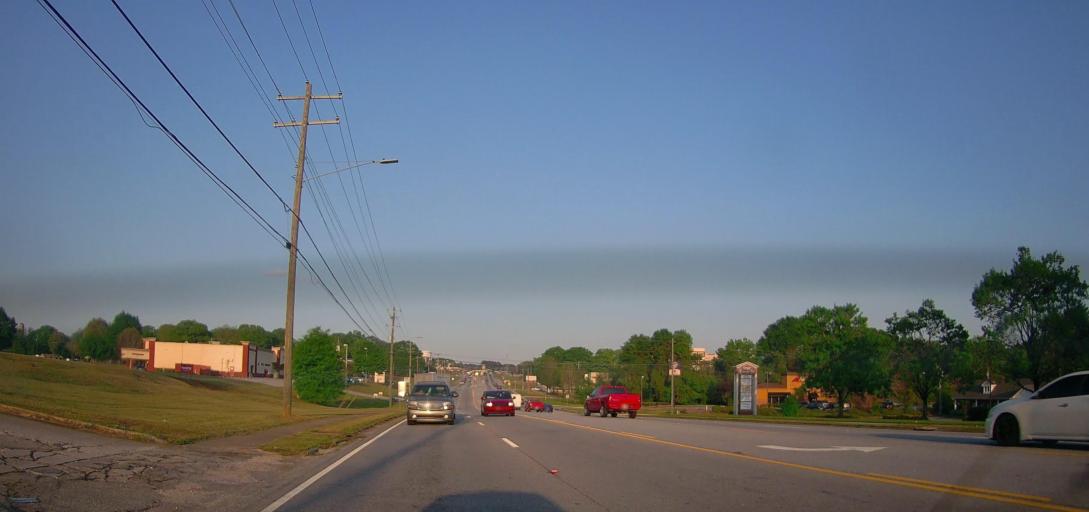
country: US
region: Georgia
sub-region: Newton County
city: Covington
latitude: 33.6031
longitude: -83.8526
